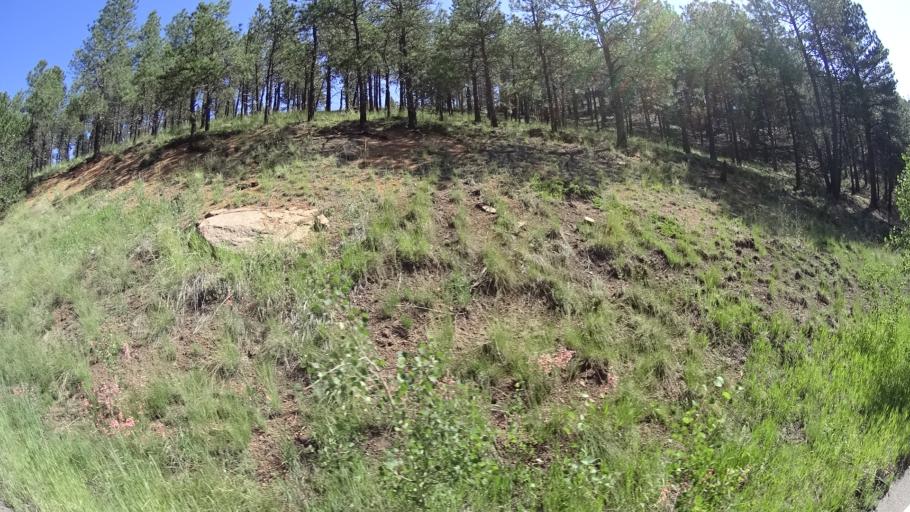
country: US
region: Colorado
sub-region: El Paso County
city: Cascade-Chipita Park
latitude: 38.9092
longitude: -105.0162
